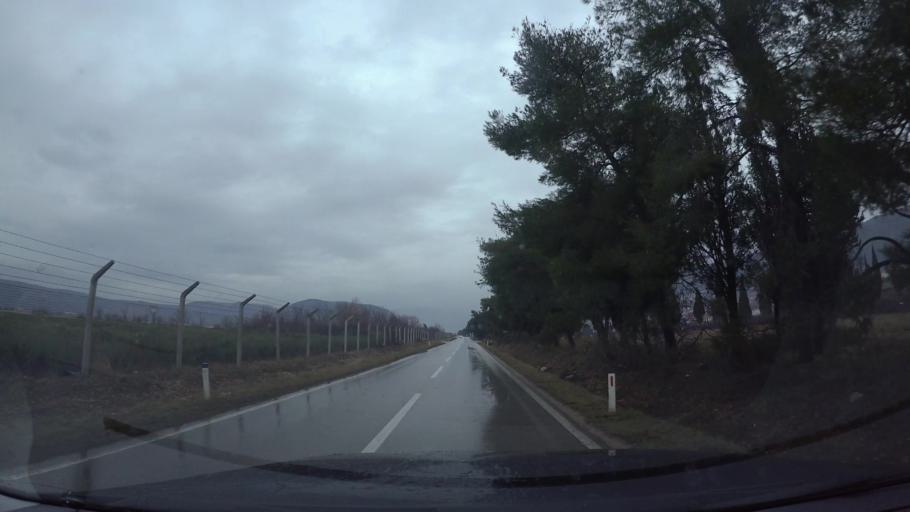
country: BA
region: Federation of Bosnia and Herzegovina
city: Rodoc
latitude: 43.2935
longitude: 17.8451
